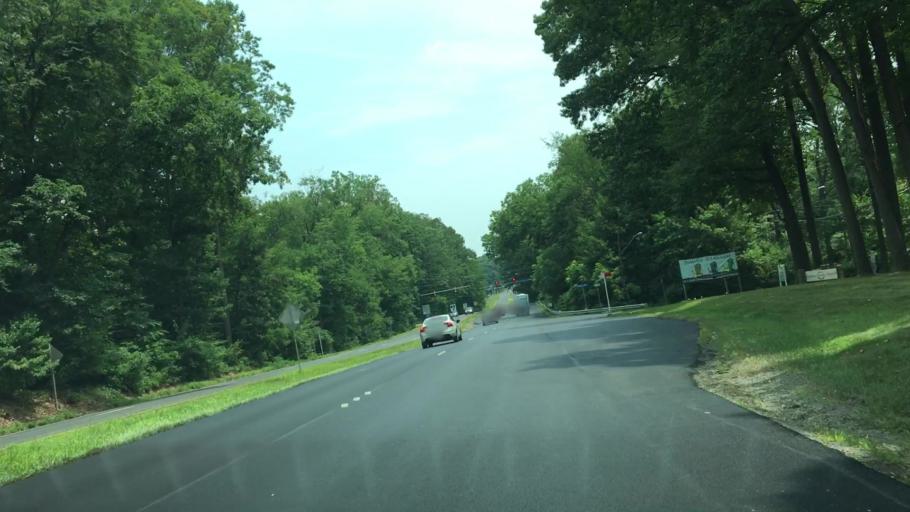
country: US
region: Virginia
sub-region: Fairfax County
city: Mantua
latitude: 38.8652
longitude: -77.2488
